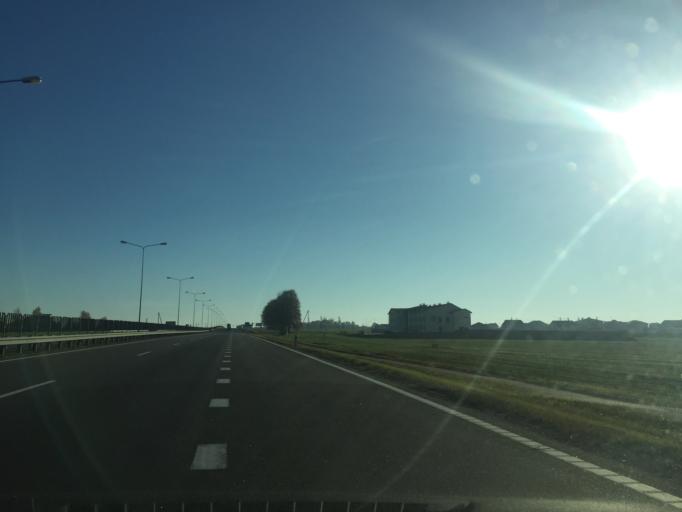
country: BY
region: Minsk
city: Smilavichy
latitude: 53.7595
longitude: 27.9894
